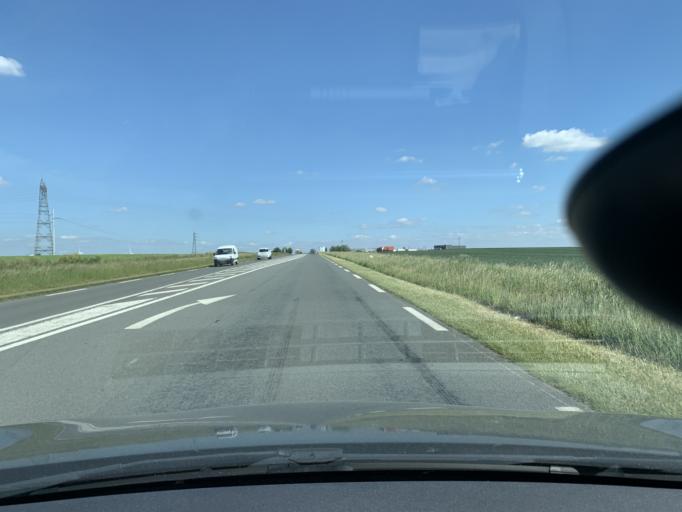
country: FR
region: Nord-Pas-de-Calais
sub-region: Departement du Nord
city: Beauvois-en-Cambresis
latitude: 50.1465
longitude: 3.3580
